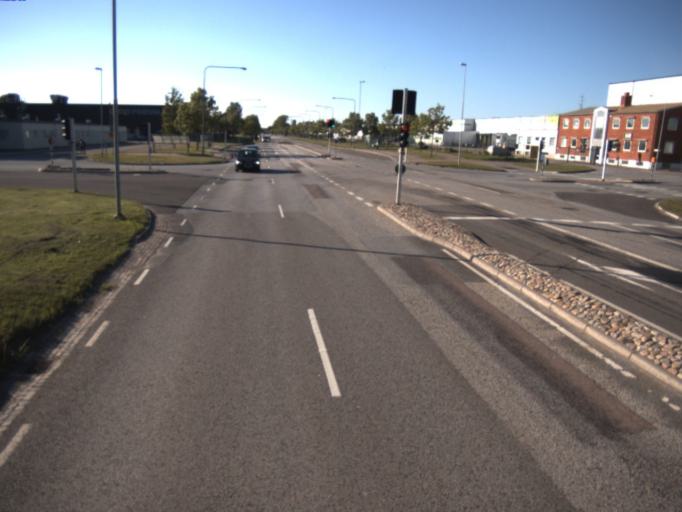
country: SE
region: Skane
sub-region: Helsingborg
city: Rydeback
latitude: 56.0091
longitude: 12.7355
